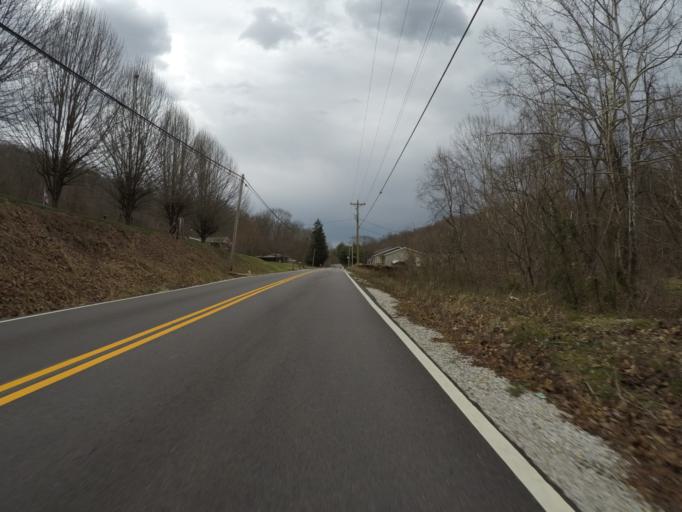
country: US
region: Ohio
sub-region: Lawrence County
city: Burlington
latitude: 38.4418
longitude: -82.5011
